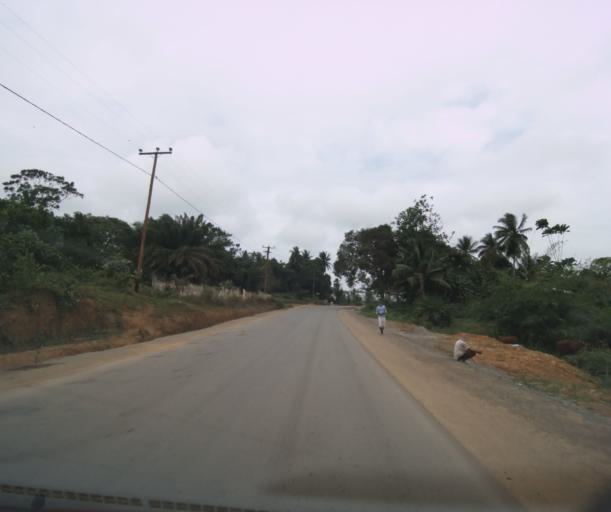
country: CM
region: South Province
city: Kribi
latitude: 2.9055
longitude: 9.9072
